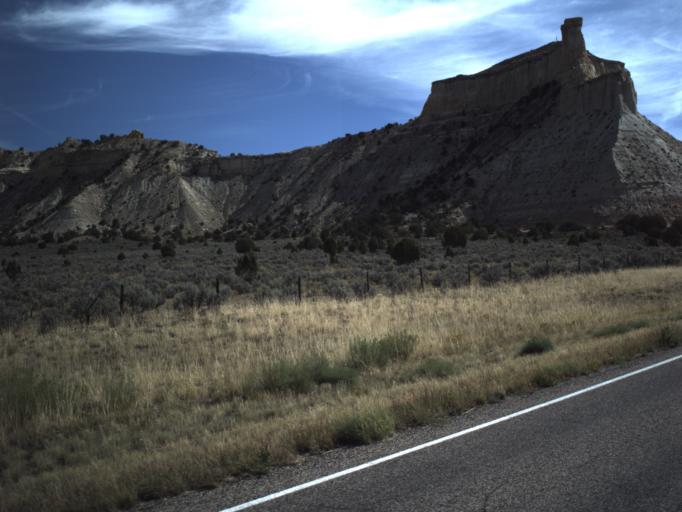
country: US
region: Utah
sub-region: Garfield County
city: Panguitch
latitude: 37.5605
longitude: -112.0258
